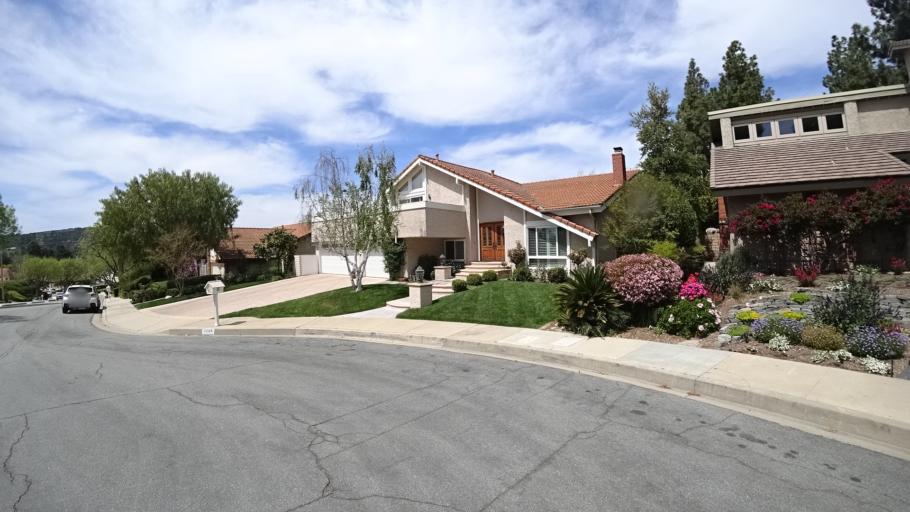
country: US
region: California
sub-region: Ventura County
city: Thousand Oaks
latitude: 34.1711
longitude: -118.8287
